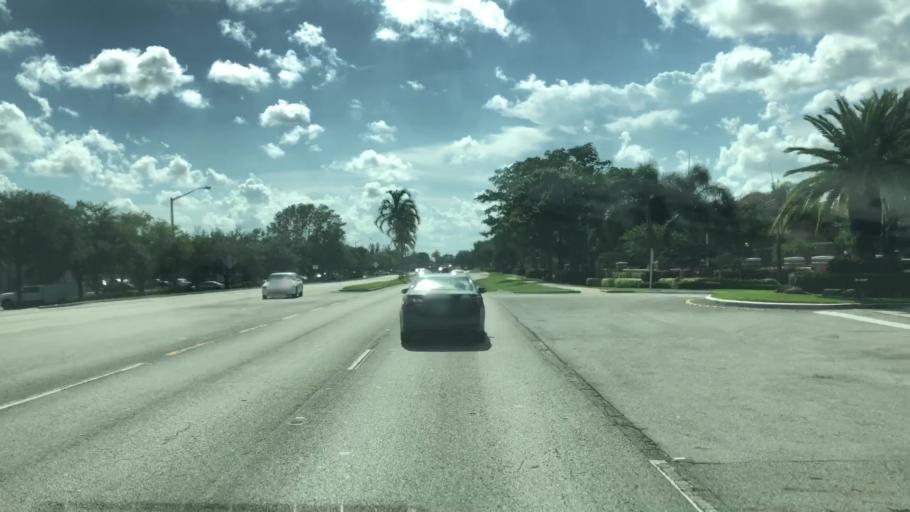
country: US
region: Florida
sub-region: Broward County
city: Parkland
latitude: 26.2870
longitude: -80.2457
